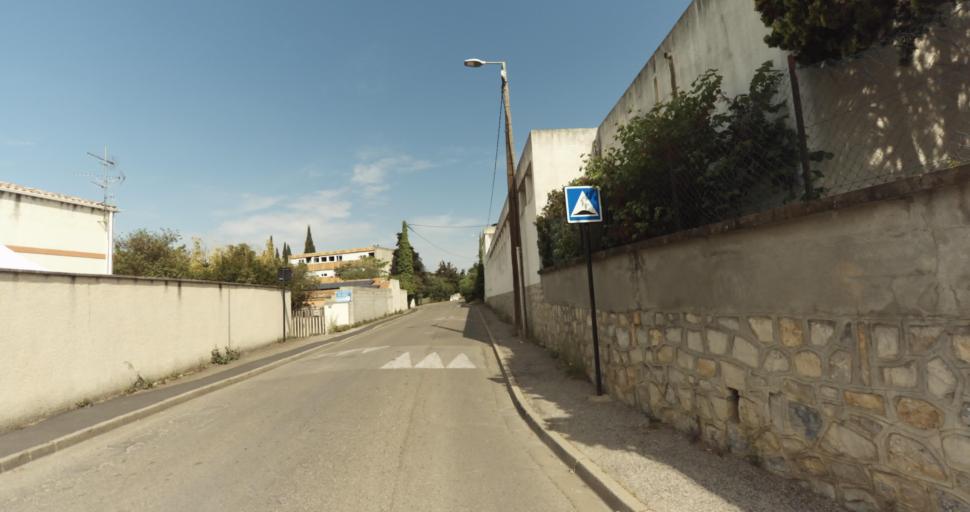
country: FR
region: Languedoc-Roussillon
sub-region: Departement du Gard
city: Rodilhan
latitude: 43.8567
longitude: 4.3964
